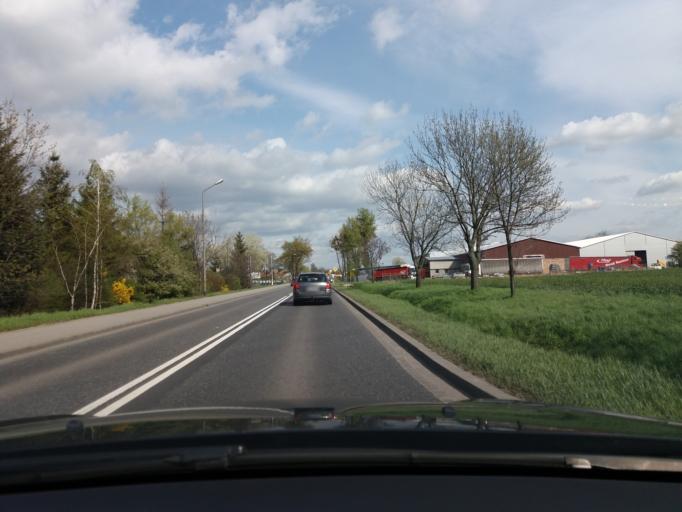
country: PL
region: Lower Silesian Voivodeship
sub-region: Powiat sredzki
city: Sroda Slaska
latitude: 51.1642
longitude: 16.6286
